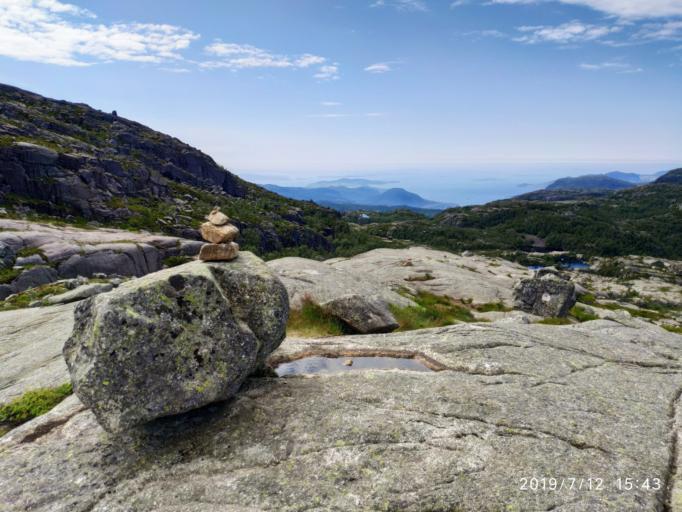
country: NO
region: Rogaland
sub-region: Forsand
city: Forsand
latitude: 58.9872
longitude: 6.1846
